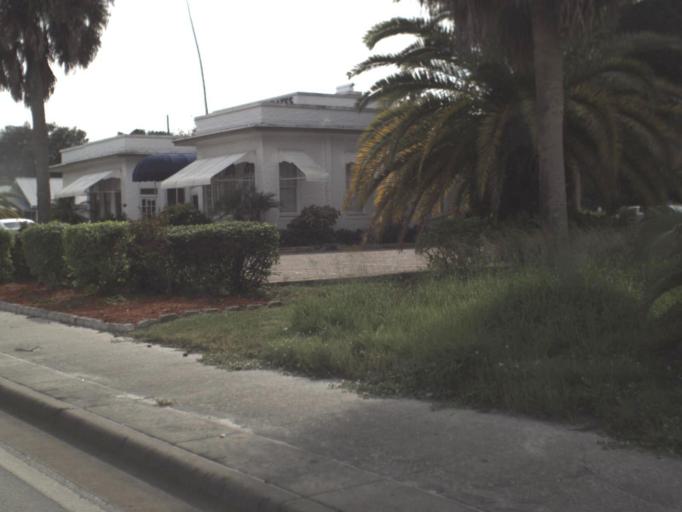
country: US
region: Florida
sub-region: Okeechobee County
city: Okeechobee
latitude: 27.2328
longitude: -80.8300
